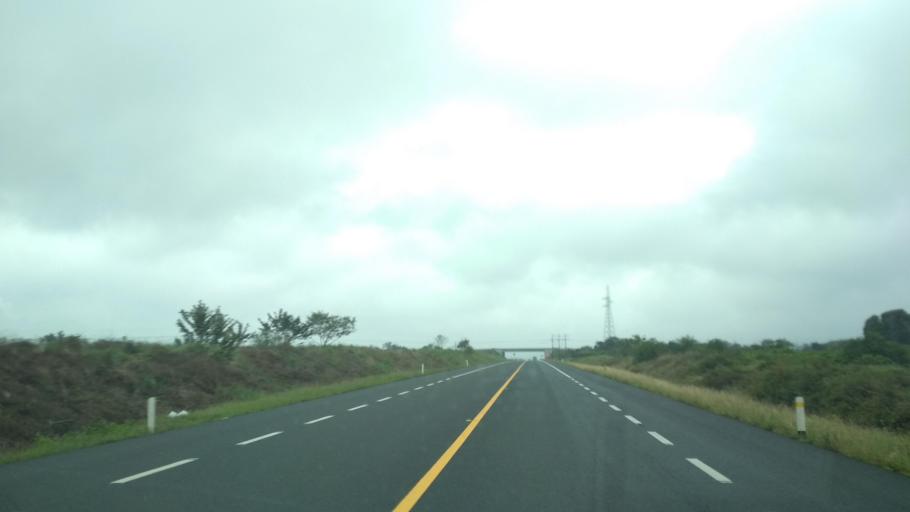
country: MX
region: Veracruz
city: Vega de San Marcos
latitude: 20.1578
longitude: -96.9527
